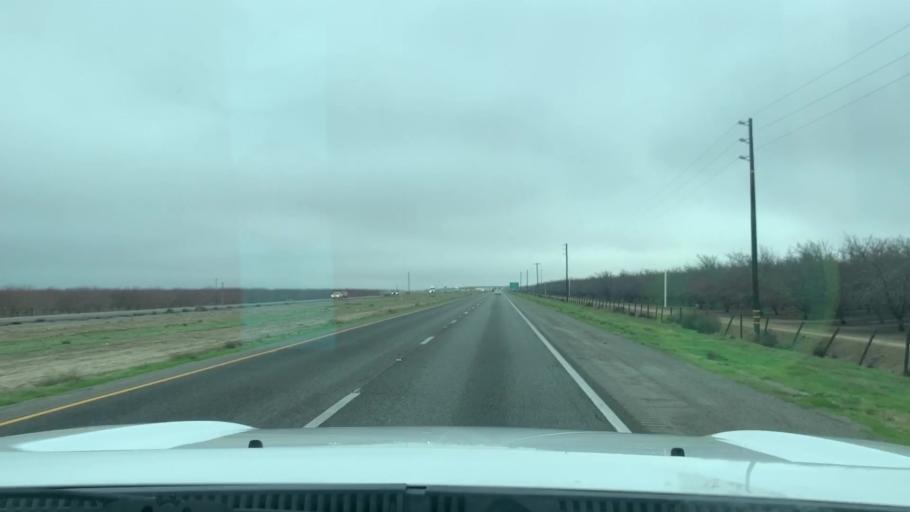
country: US
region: California
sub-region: Kern County
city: Buttonwillow
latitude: 35.4645
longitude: -119.4877
